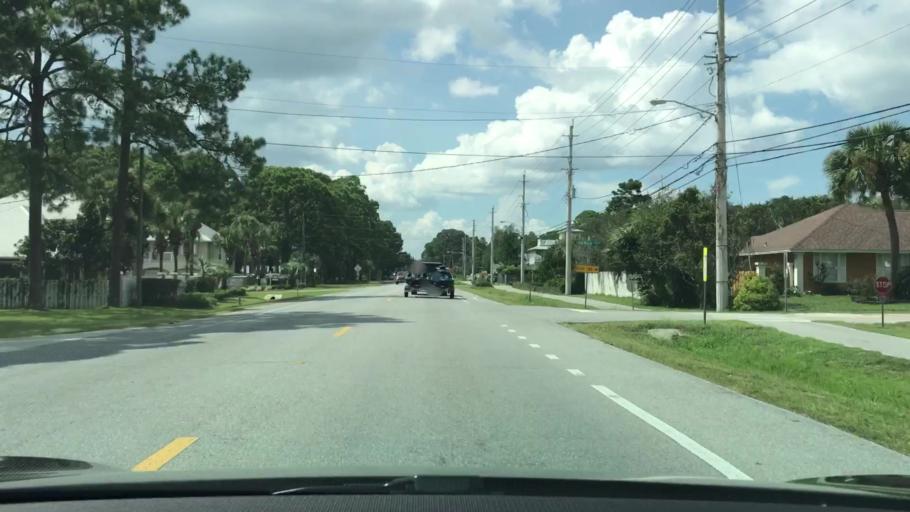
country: US
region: Florida
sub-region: Bay County
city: Lower Grand Lagoon
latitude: 30.1602
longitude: -85.7633
